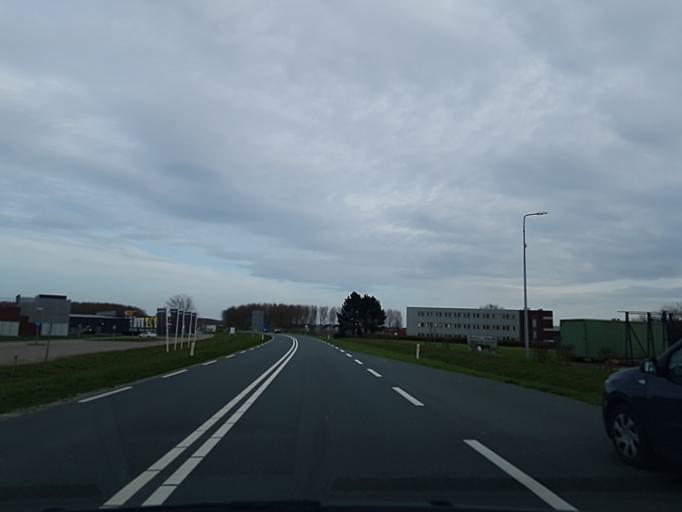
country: NL
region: Zeeland
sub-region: Gemeente Hulst
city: Hulst
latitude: 51.2721
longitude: 4.0427
